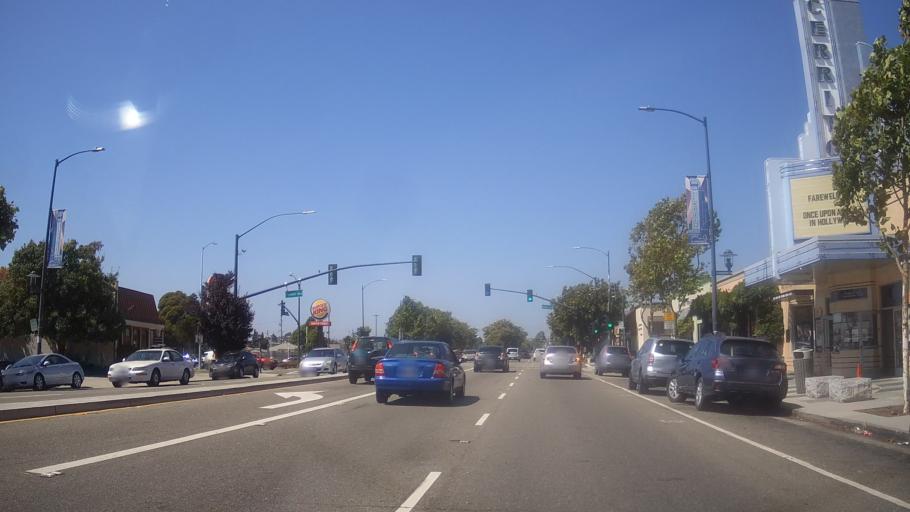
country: US
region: California
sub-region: Alameda County
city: Albany
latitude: 37.9017
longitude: -122.3029
